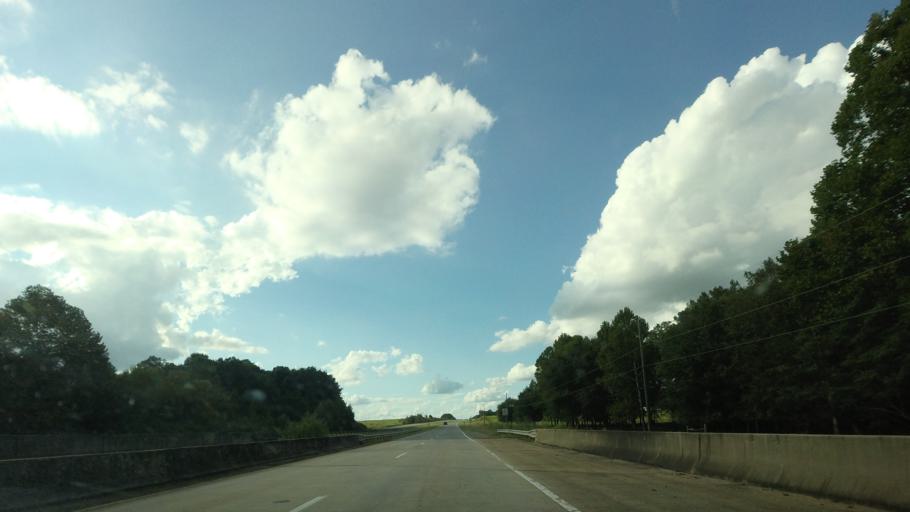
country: US
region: Georgia
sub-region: Houston County
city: Perry
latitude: 32.4270
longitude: -83.7143
